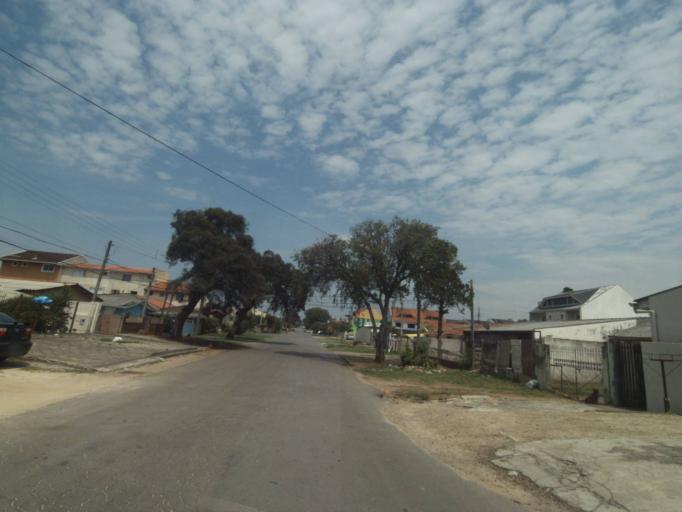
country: BR
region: Parana
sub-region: Pinhais
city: Pinhais
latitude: -25.4238
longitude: -49.1988
